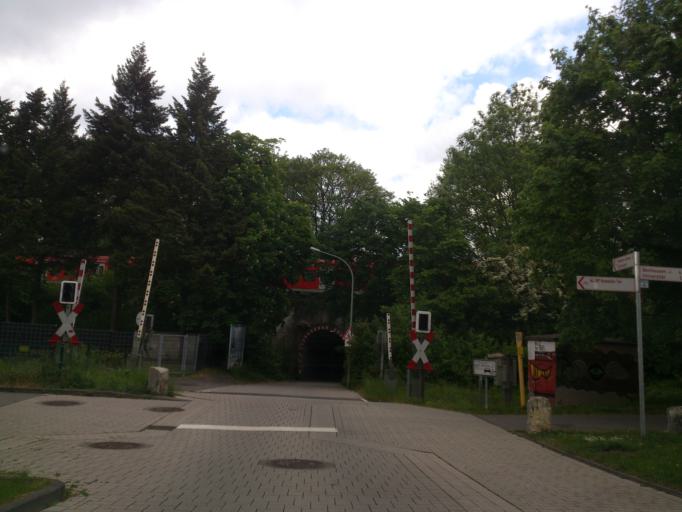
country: DE
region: North Rhine-Westphalia
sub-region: Regierungsbezirk Detmold
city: Paderborn
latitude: 51.7164
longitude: 8.7676
